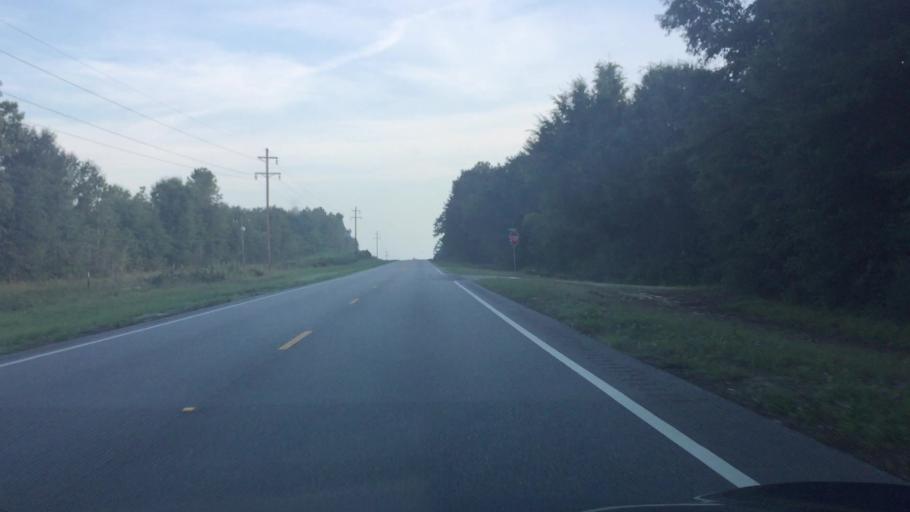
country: US
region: Alabama
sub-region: Covington County
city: Florala
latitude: 31.0667
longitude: -86.4004
